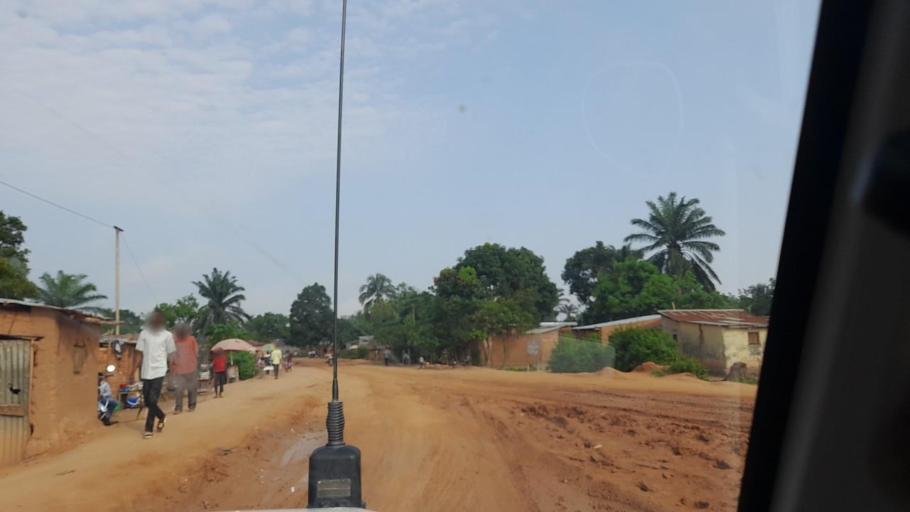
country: CD
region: Kasai-Occidental
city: Kananga
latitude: -5.8908
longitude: 22.3743
